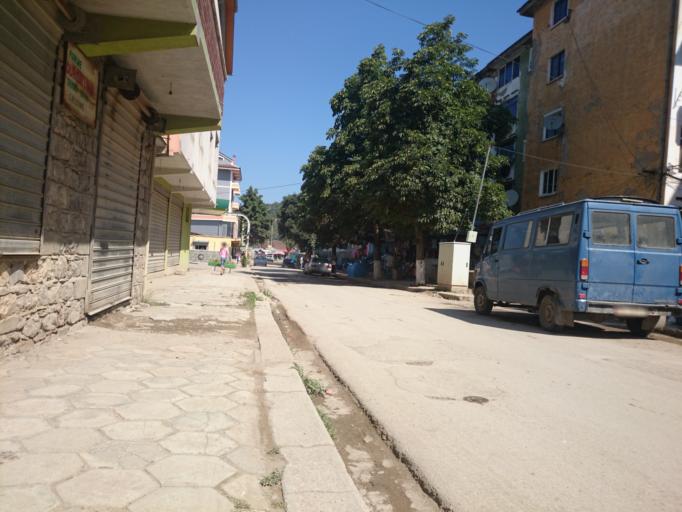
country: AL
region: Diber
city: Peshkopi
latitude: 41.6846
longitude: 20.4255
